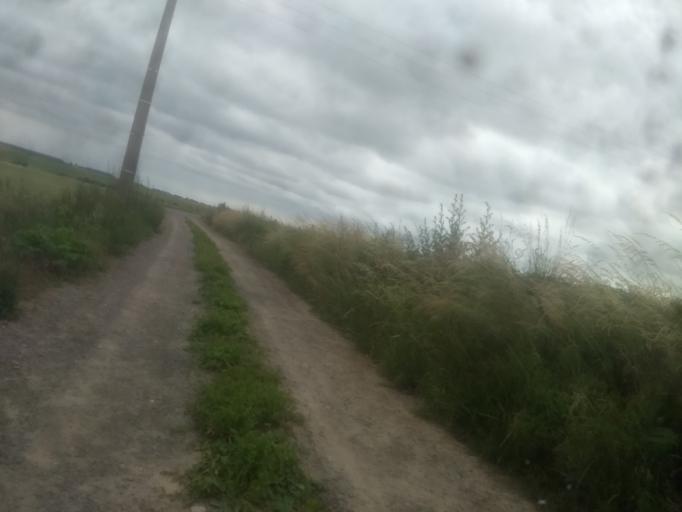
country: FR
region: Nord-Pas-de-Calais
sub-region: Departement du Pas-de-Calais
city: Neuville-Saint-Vaast
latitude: 50.3456
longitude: 2.7410
